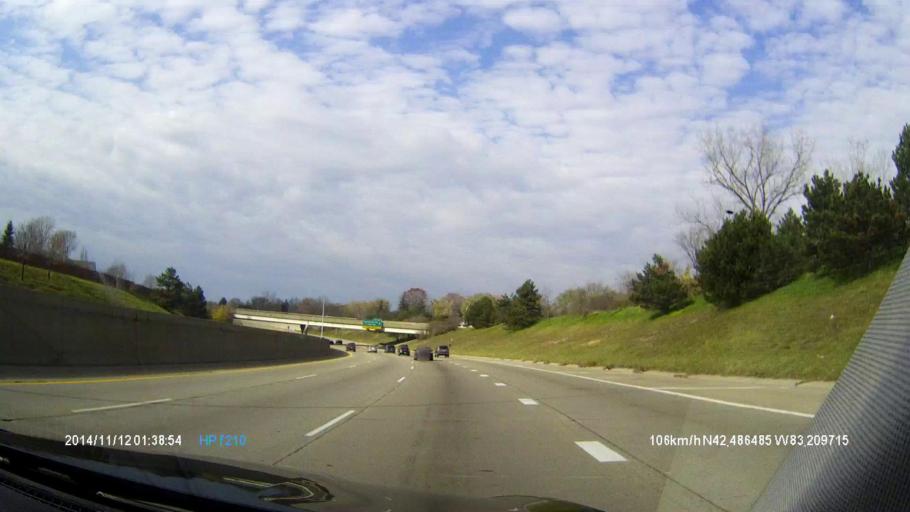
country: US
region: Michigan
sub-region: Oakland County
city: Lathrup Village
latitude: 42.4866
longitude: -83.2099
